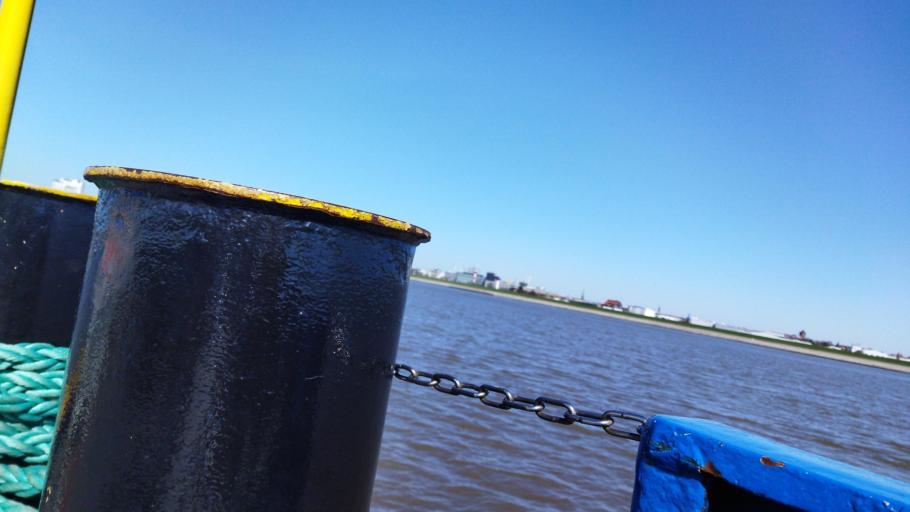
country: DE
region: Bremen
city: Bremerhaven
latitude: 53.5281
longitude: 8.5662
